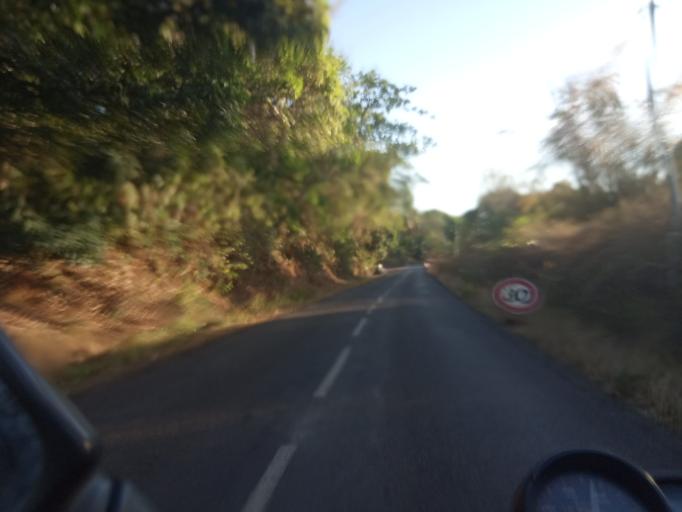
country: YT
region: Kani-Keli
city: Kani Keli
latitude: -12.9355
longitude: 45.1036
